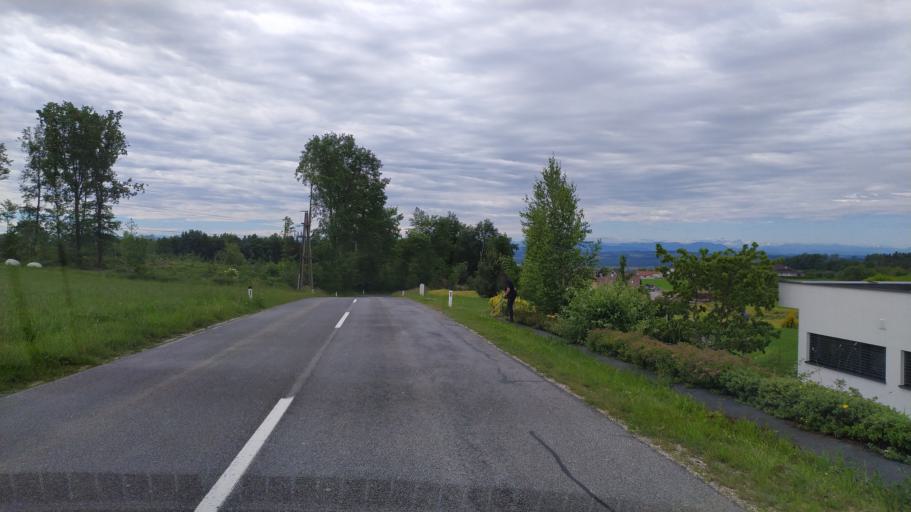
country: AT
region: Upper Austria
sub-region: Politischer Bezirk Perg
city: Perg
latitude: 48.2632
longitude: 14.6520
